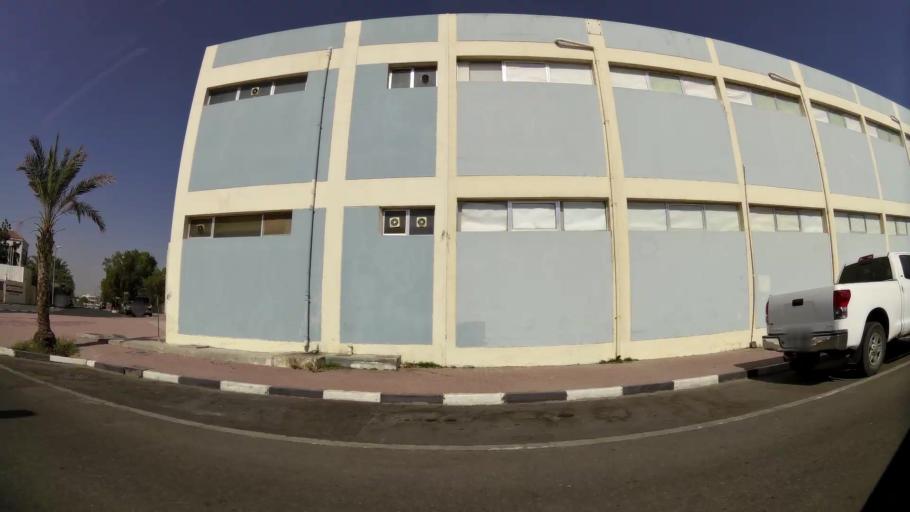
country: AE
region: Ash Shariqah
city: Sharjah
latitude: 25.2462
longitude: 55.2888
